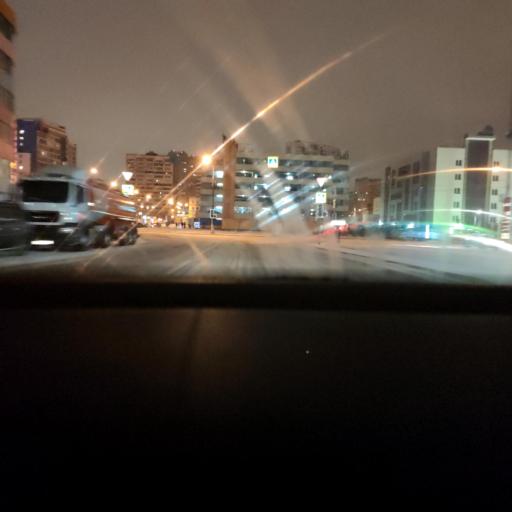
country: RU
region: Moscow
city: Strogino
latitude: 55.7918
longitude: 37.3906
